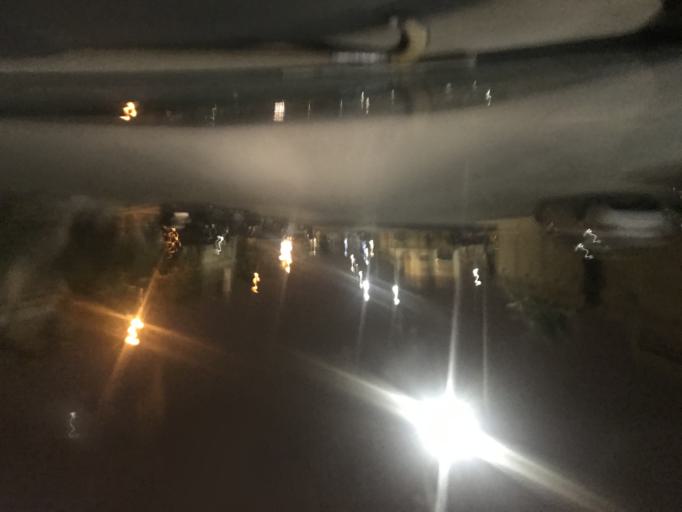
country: SA
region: Ar Riyad
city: Riyadh
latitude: 24.7980
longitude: 46.7000
